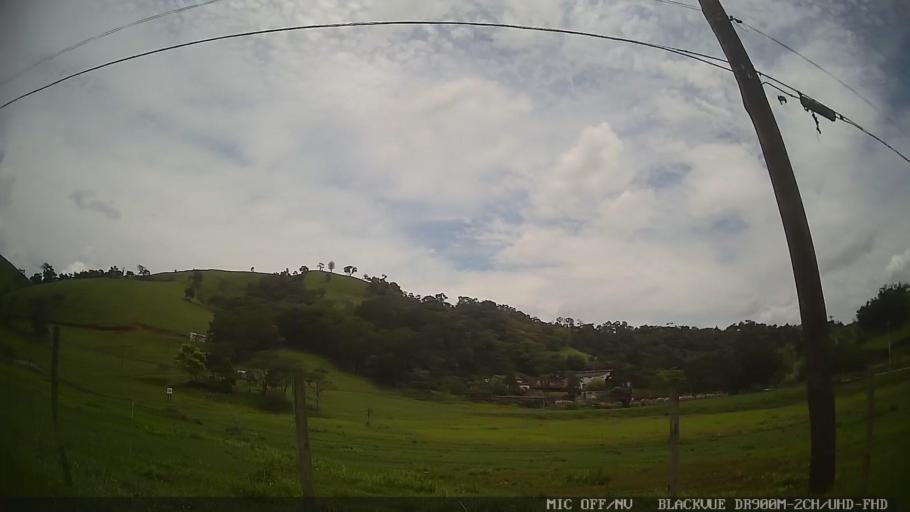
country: BR
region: Sao Paulo
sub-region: Santa Isabel
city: Santa Isabel
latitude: -23.3470
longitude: -46.2187
